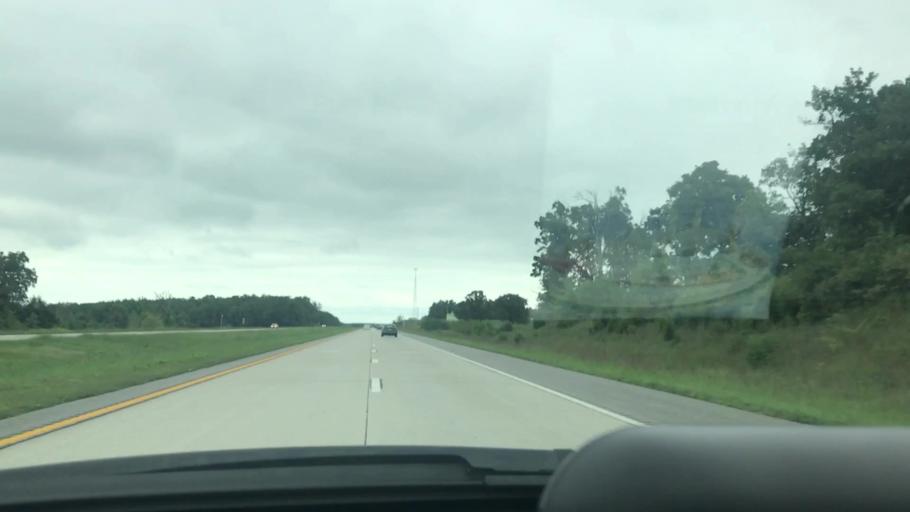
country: US
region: Missouri
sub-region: Greene County
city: Fair Grove
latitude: 37.4984
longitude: -93.1389
